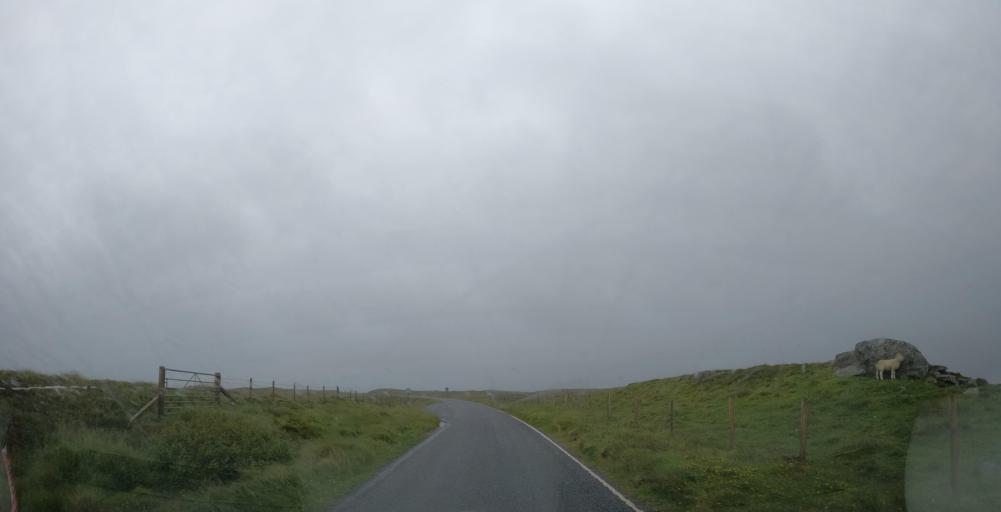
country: GB
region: Scotland
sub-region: Eilean Siar
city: Barra
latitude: 57.0076
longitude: -7.4117
